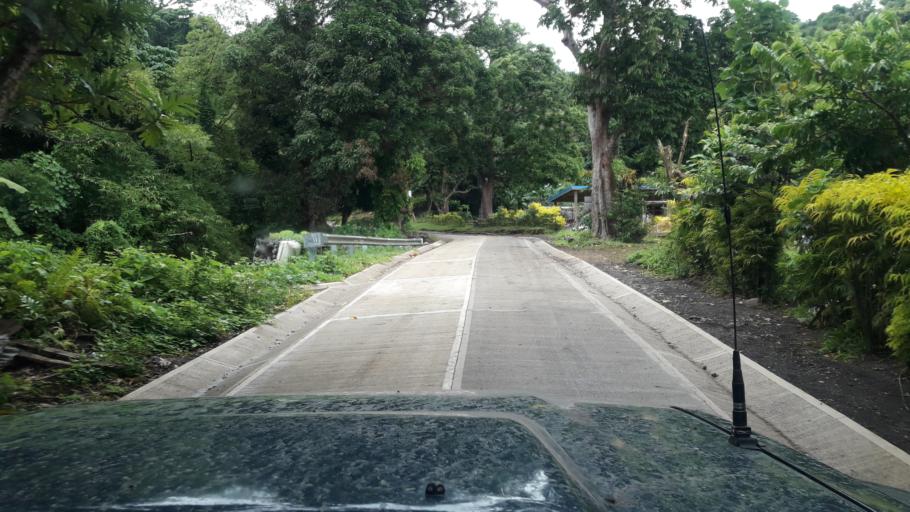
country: VU
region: Shefa
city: Port-Vila
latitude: -16.9103
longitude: 168.5297
